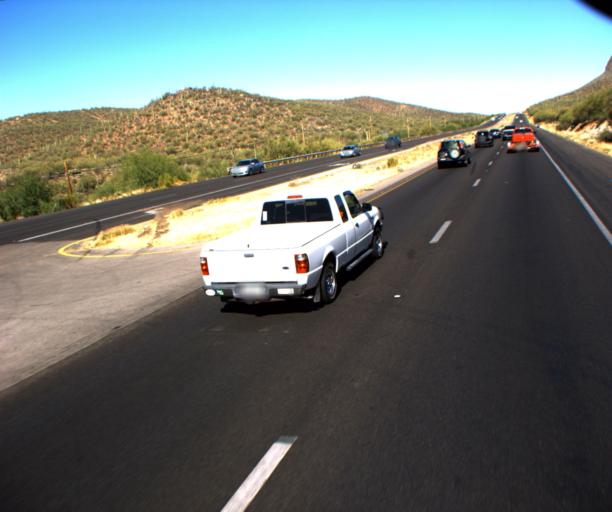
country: US
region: Arizona
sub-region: Pima County
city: Drexel Heights
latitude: 32.1768
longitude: -111.0287
